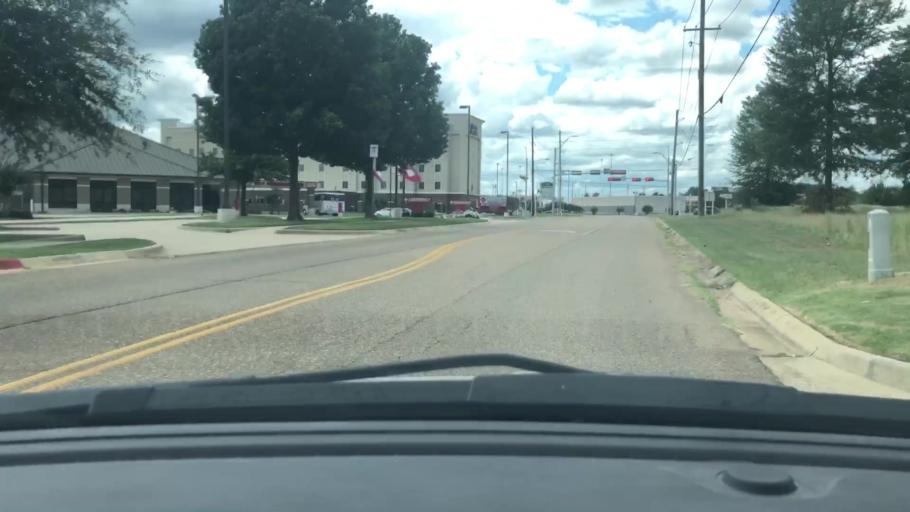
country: US
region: Arkansas
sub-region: Miller County
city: Texarkana
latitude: 33.4587
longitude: -94.0750
